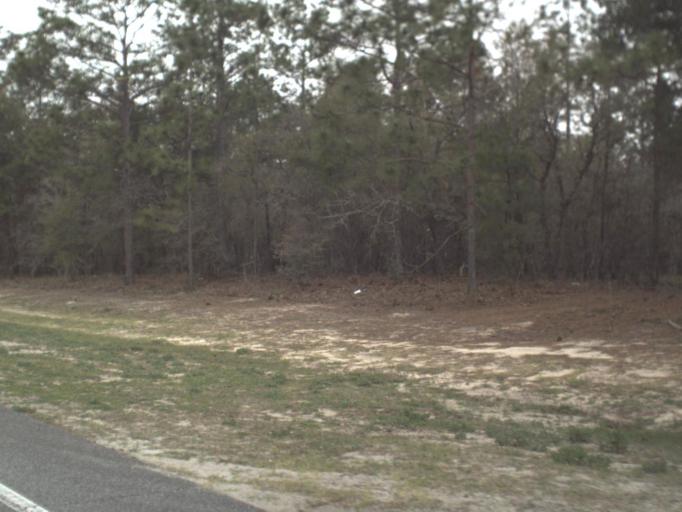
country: US
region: Florida
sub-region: Wakulla County
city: Crawfordville
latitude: 30.1335
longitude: -84.3416
